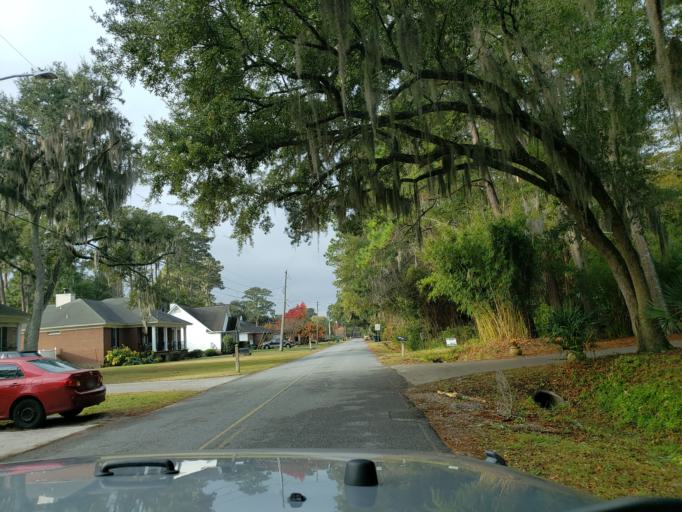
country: US
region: Georgia
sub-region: Chatham County
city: Wilmington Island
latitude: 32.0148
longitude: -80.9608
